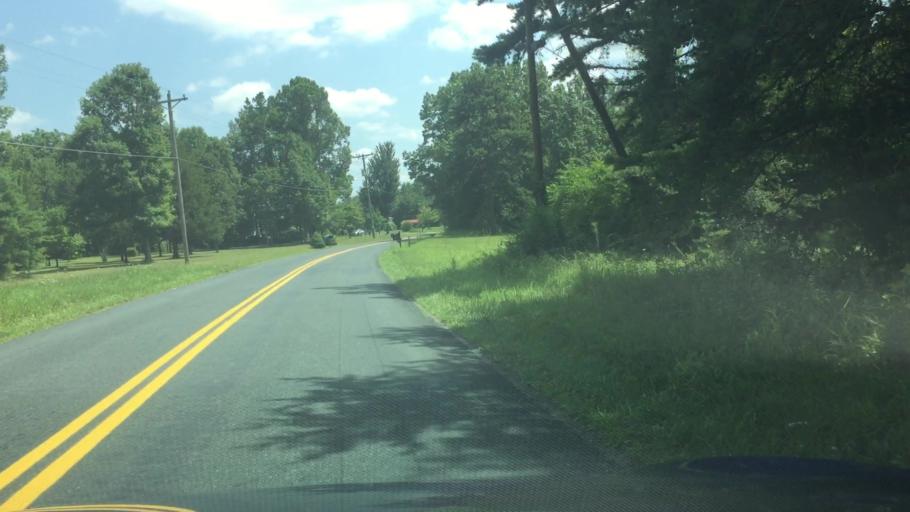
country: US
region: Virginia
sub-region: Appomattox County
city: Appomattox
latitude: 37.3040
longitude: -78.8488
